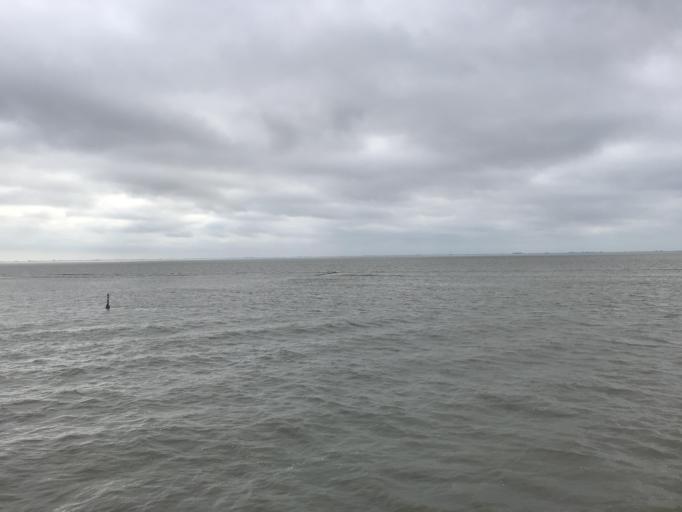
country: DE
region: Lower Saxony
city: Emden
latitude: 53.3298
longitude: 7.1081
